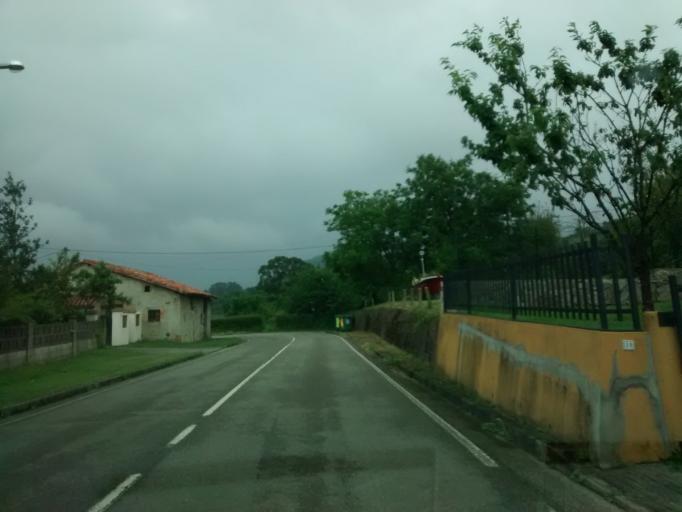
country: ES
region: Asturias
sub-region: Province of Asturias
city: Villaviciosa
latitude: 43.5210
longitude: -5.3692
